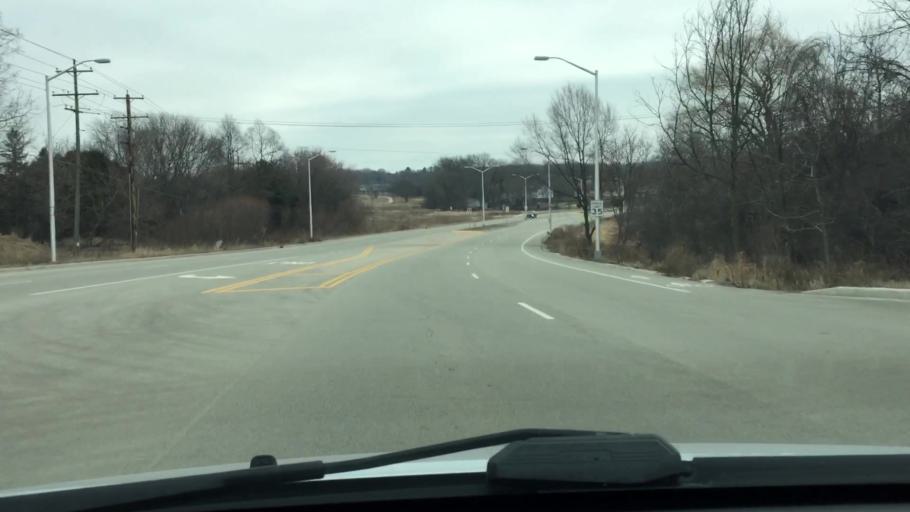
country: US
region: Wisconsin
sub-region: Waukesha County
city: Waukesha
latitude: 42.9886
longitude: -88.2161
